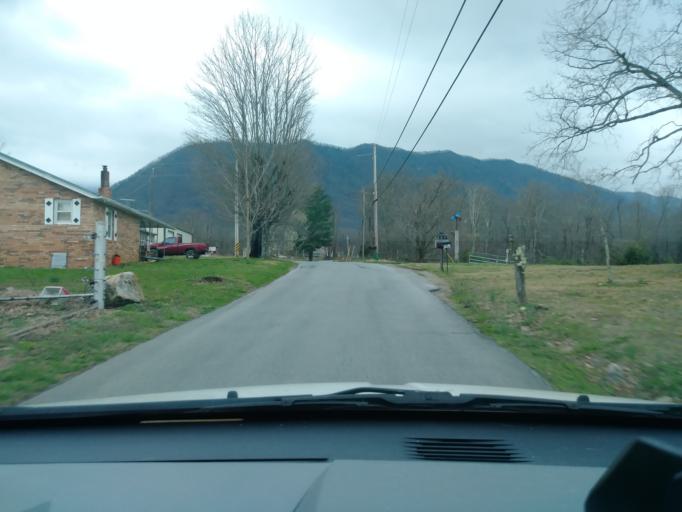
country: US
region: Tennessee
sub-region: Greene County
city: Tusculum
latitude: 36.0776
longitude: -82.7245
